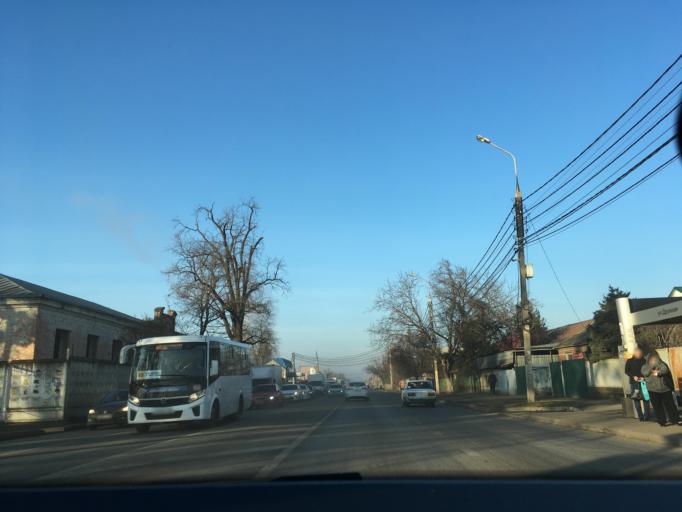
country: RU
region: Krasnodarskiy
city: Krasnodar
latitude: 45.0894
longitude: 39.0142
